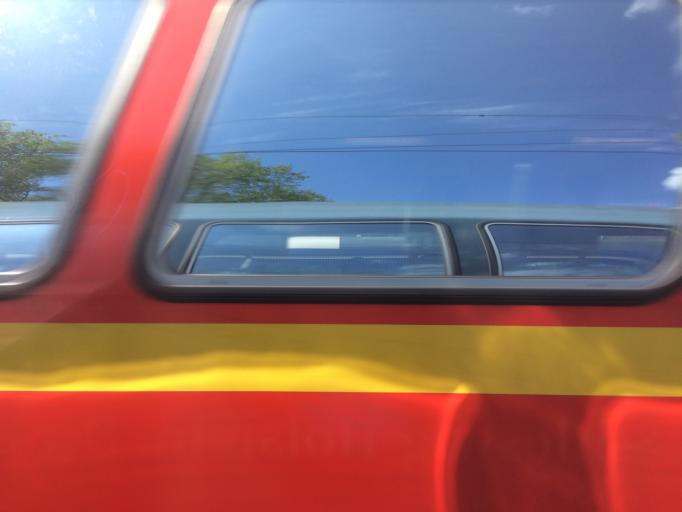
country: DE
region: Schleswig-Holstein
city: Elmshorn
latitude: 53.7542
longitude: 9.6594
